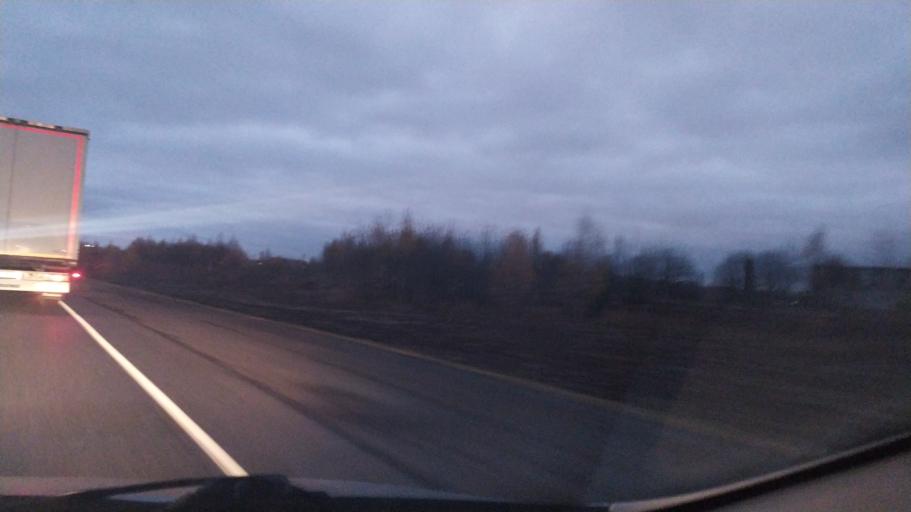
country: RU
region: Chuvashia
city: Kugesi
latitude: 56.0536
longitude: 47.2763
